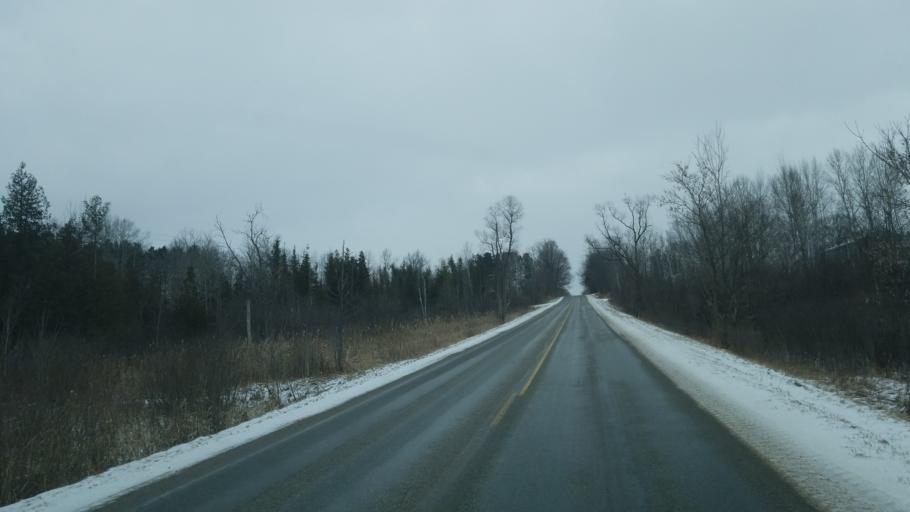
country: US
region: Michigan
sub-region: Osceola County
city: Evart
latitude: 43.9279
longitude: -85.2465
